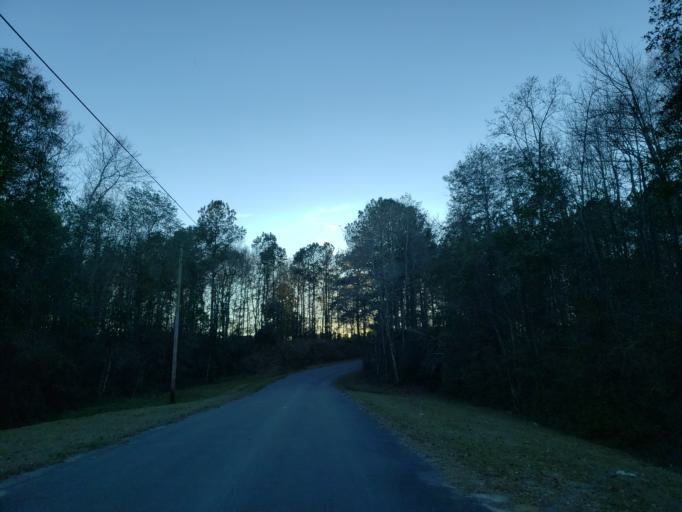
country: US
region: Mississippi
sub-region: Covington County
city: Collins
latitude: 31.5725
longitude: -89.4539
